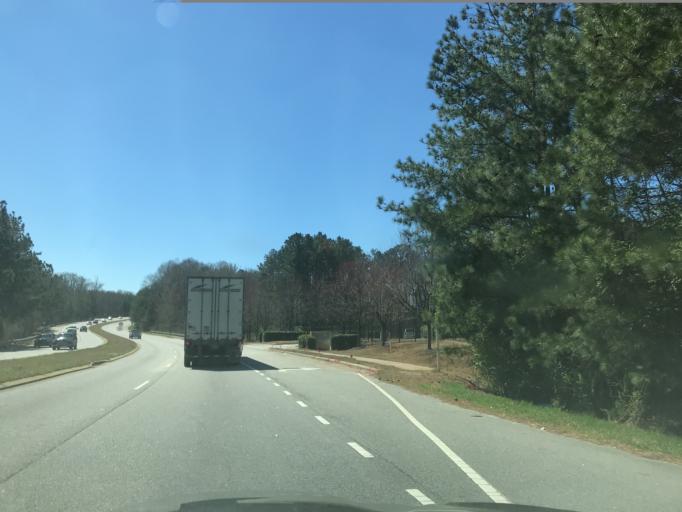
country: US
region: North Carolina
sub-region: Wake County
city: Raleigh
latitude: 35.7404
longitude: -78.6410
